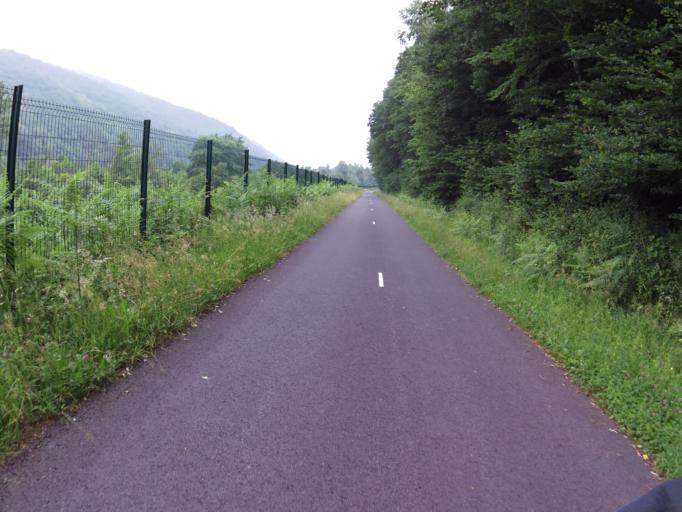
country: FR
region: Champagne-Ardenne
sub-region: Departement des Ardennes
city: Revin
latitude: 49.9565
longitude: 4.6572
